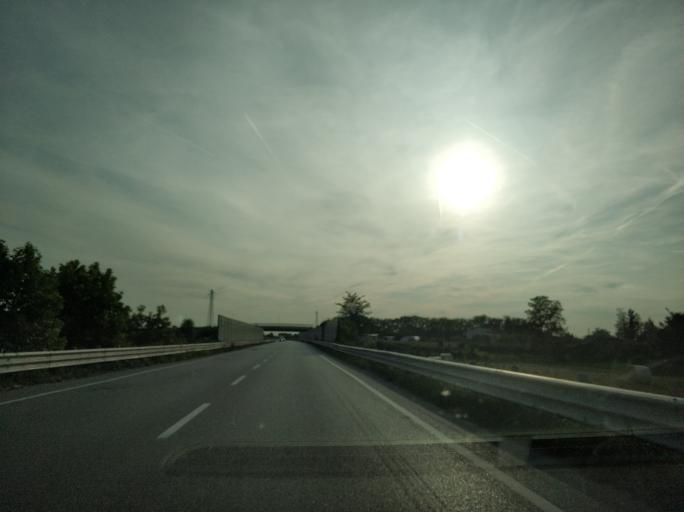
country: IT
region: Veneto
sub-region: Provincia di Padova
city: Sant'Elena
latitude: 45.2127
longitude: 11.7090
